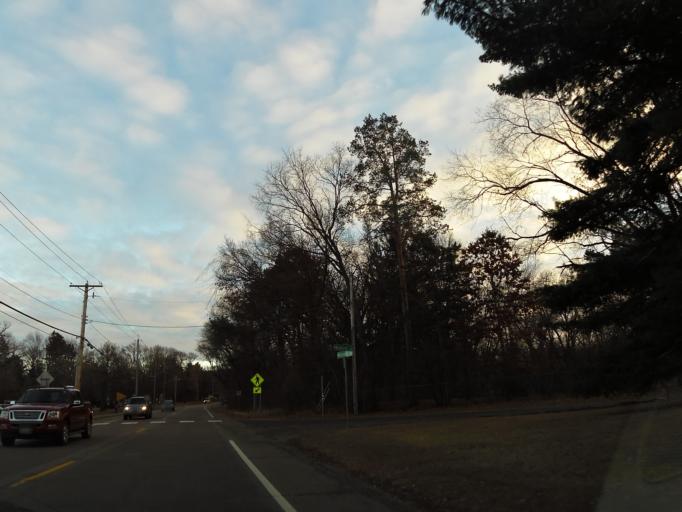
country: US
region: Minnesota
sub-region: Washington County
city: Mahtomedi
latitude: 45.0731
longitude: -92.9575
